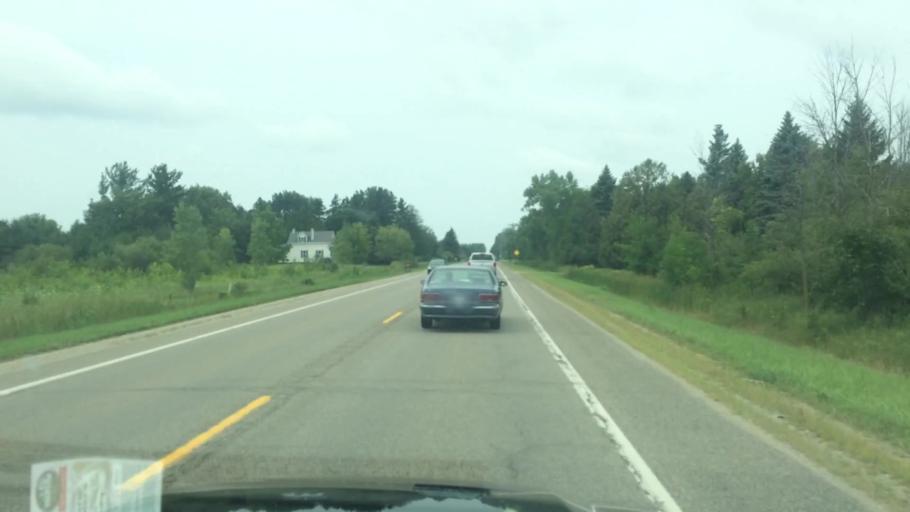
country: US
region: Michigan
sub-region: Huron County
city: Bad Axe
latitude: 43.8850
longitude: -83.0030
